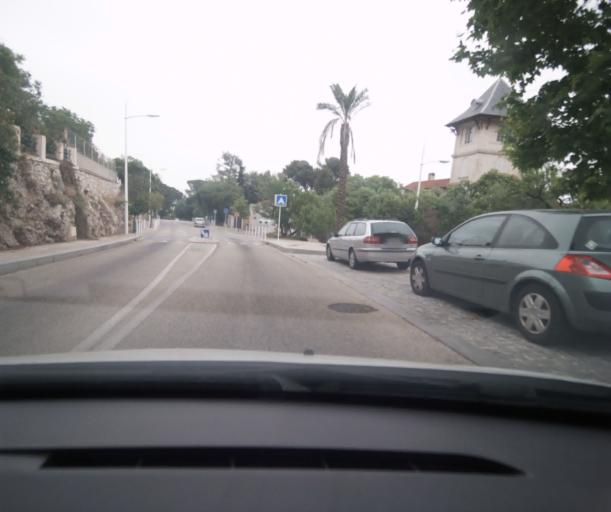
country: FR
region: Provence-Alpes-Cote d'Azur
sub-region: Departement du Var
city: La Valette-du-Var
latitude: 43.1356
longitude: 5.9694
